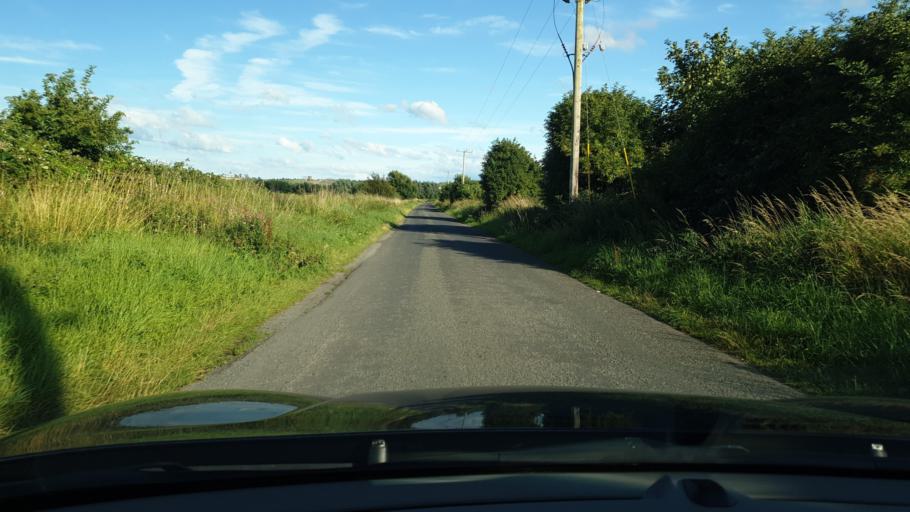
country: IE
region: Leinster
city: Balrothery
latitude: 53.5801
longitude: -6.2270
